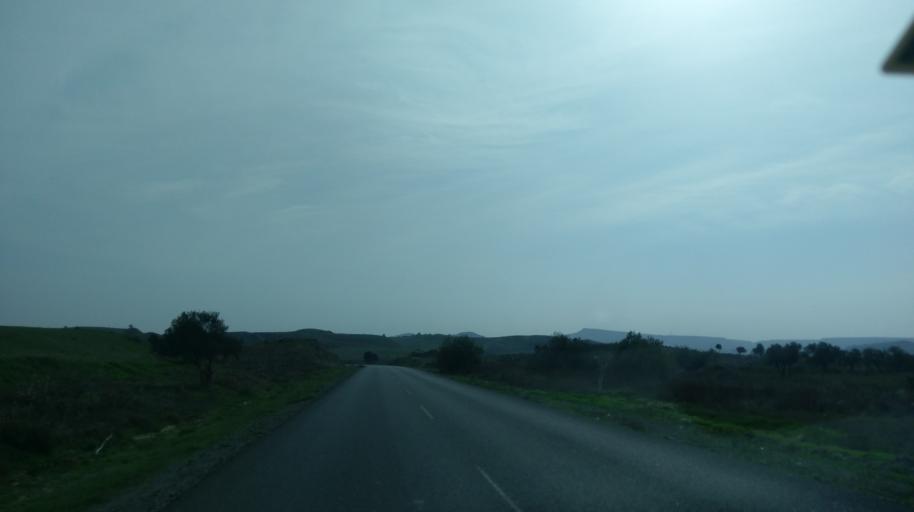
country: CY
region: Keryneia
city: Lapithos
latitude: 35.2838
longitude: 33.0941
